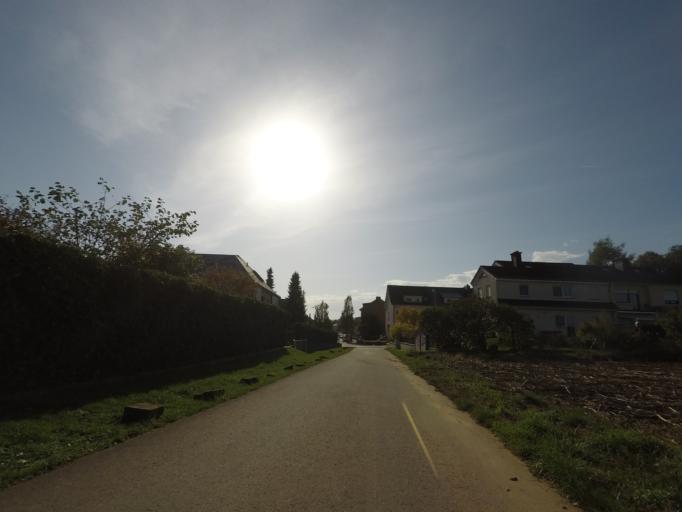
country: LU
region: Luxembourg
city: Itzig
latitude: 49.5900
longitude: 6.1734
